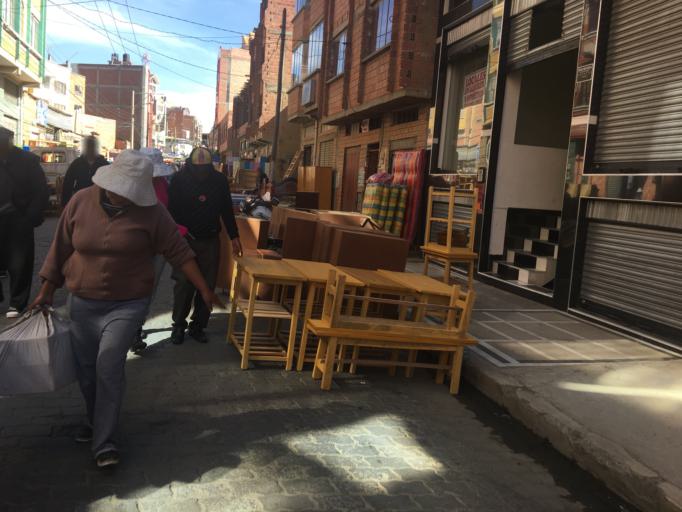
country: BO
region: La Paz
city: La Paz
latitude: -16.4899
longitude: -68.1714
